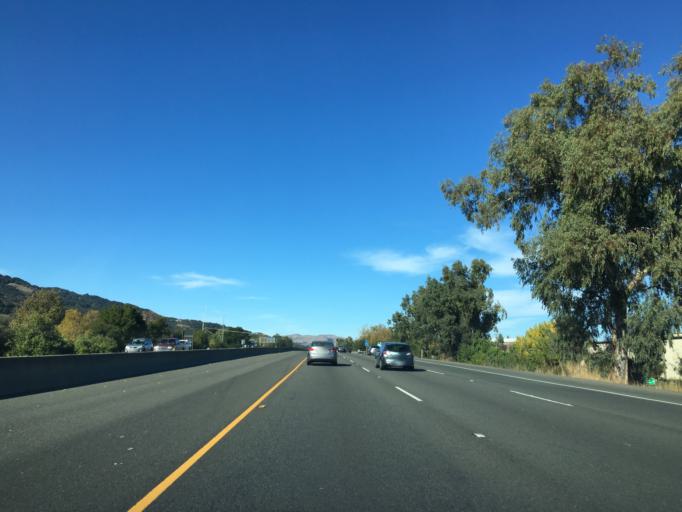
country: US
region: California
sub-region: Alameda County
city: Pleasanton
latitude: 37.6549
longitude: -121.8995
